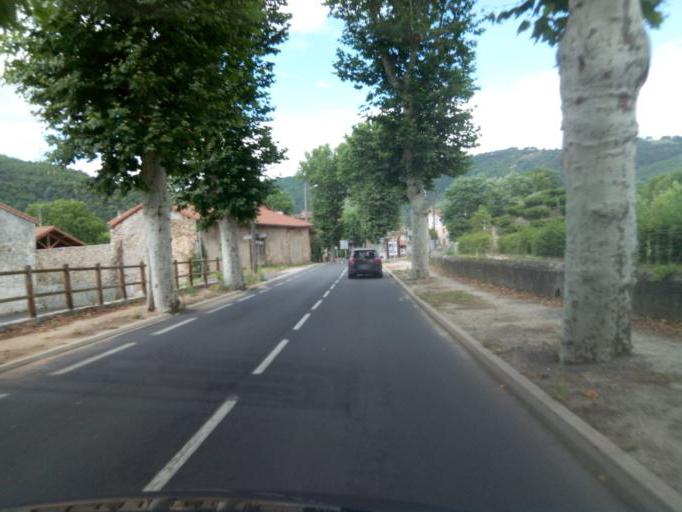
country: FR
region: Auvergne
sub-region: Departement de la Haute-Loire
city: Chadrac
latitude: 45.1215
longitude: 3.9089
